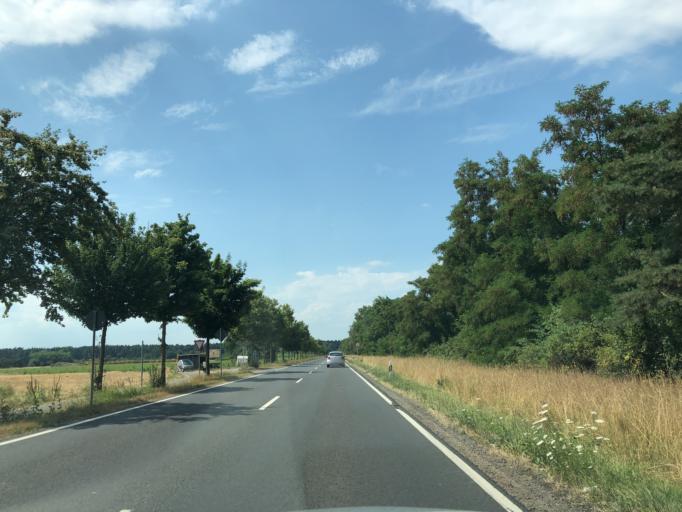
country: DE
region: Hesse
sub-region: Regierungsbezirk Darmstadt
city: Babenhausen
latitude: 49.9724
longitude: 8.9439
